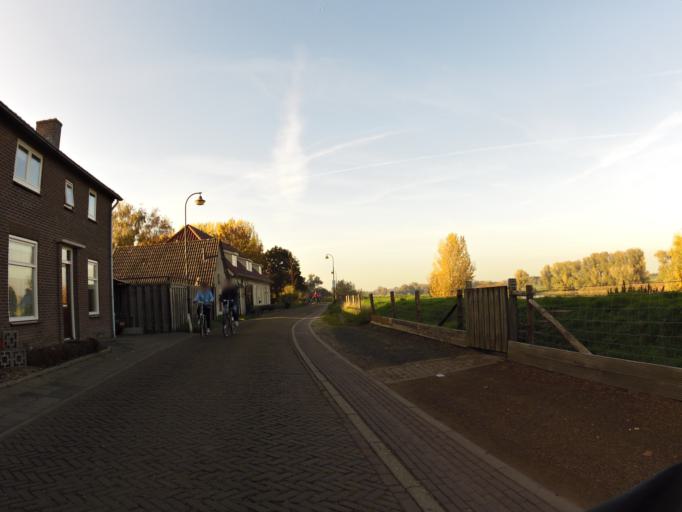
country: NL
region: Gelderland
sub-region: Gemeente Maasdriel
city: Hedel
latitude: 51.7359
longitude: 5.2390
